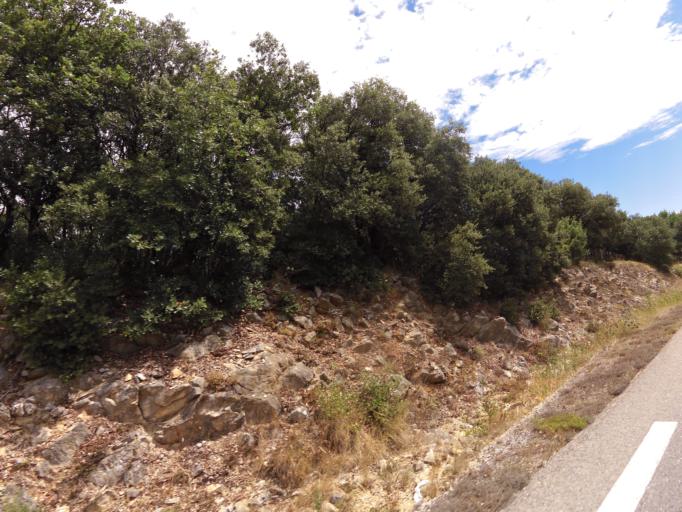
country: FR
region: Languedoc-Roussillon
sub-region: Departement du Gard
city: Quissac
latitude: 43.8726
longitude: 4.0152
